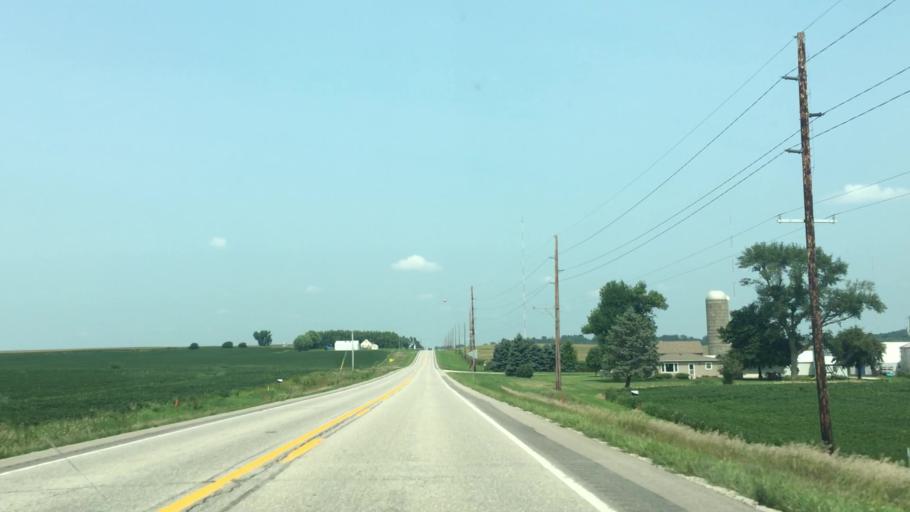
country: US
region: Iowa
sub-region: Benton County
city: Urbana
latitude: 42.2704
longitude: -91.8904
